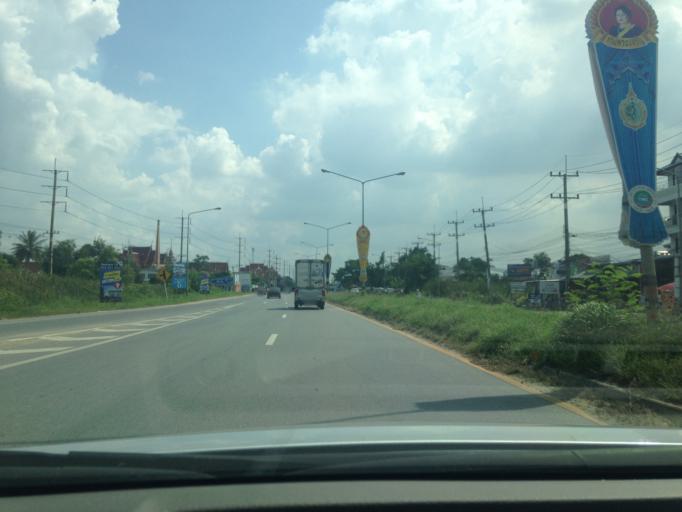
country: TH
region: Pathum Thani
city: Sam Khok
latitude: 14.0820
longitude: 100.5203
